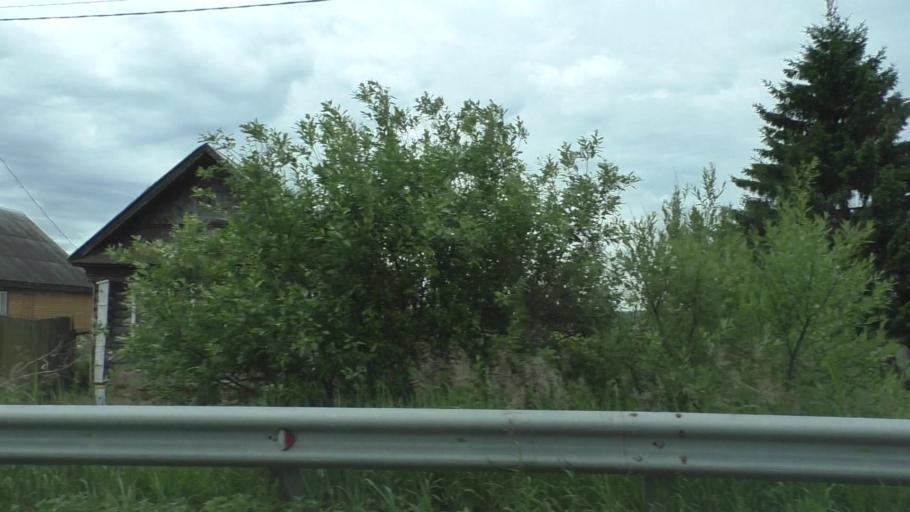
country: RU
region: Moskovskaya
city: Imeni Tsyurupy
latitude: 55.5043
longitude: 38.7786
